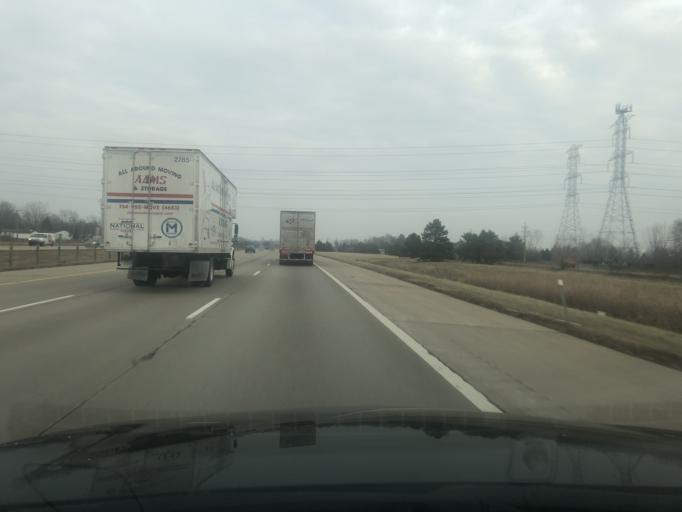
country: US
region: Michigan
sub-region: Wayne County
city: Belleville
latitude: 42.2198
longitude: -83.4569
